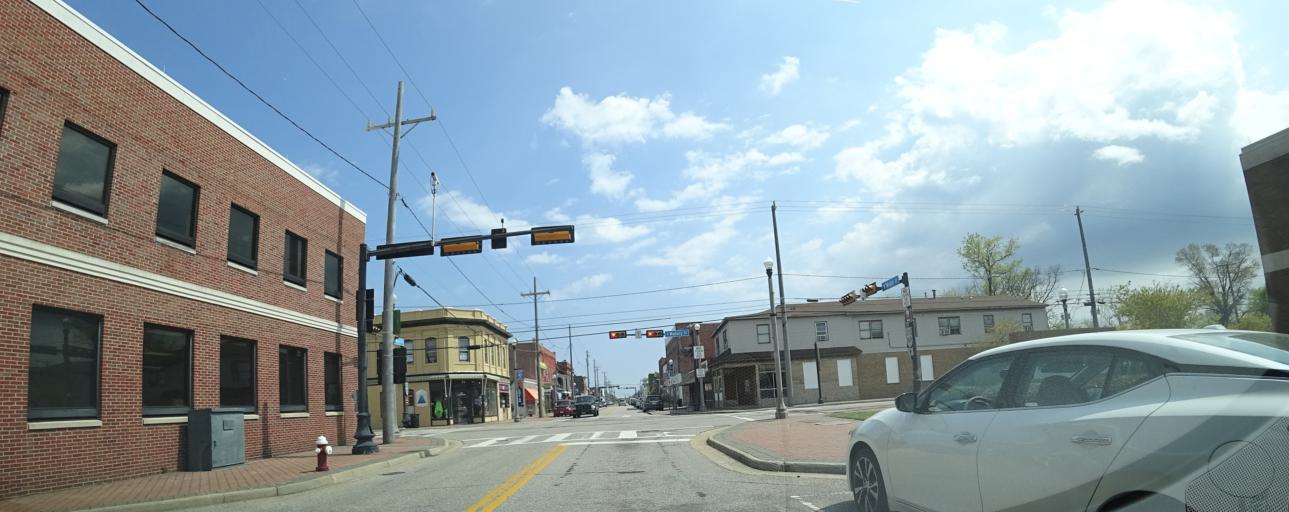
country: US
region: Virginia
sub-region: City of Hampton
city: East Hampton
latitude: 37.0188
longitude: -76.3226
